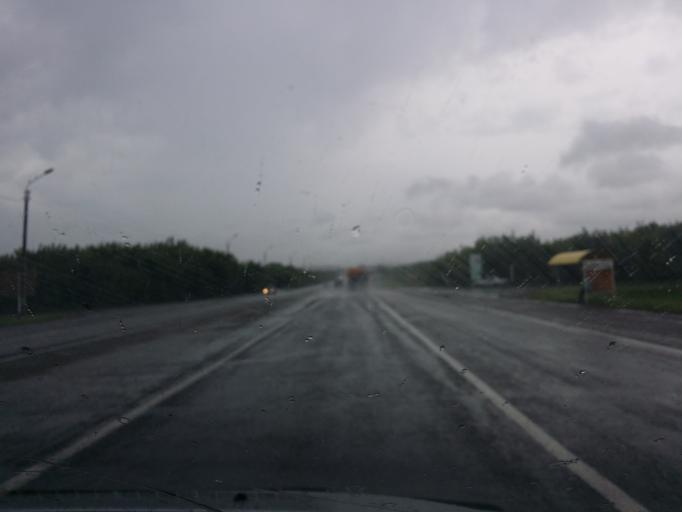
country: RU
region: Altai Krai
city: Novosilikatnyy
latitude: 53.3509
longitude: 83.5952
